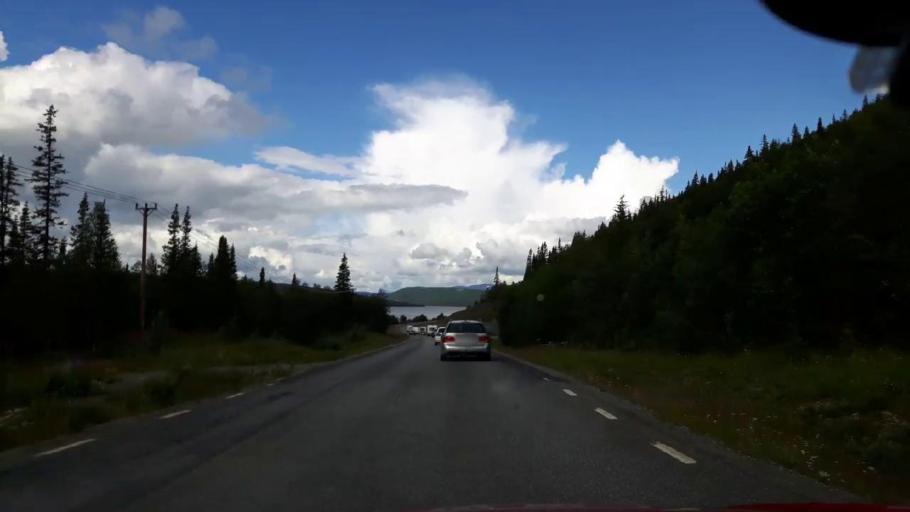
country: SE
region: Vaesterbotten
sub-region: Vilhelmina Kommun
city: Sjoberg
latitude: 65.0379
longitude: 15.1267
